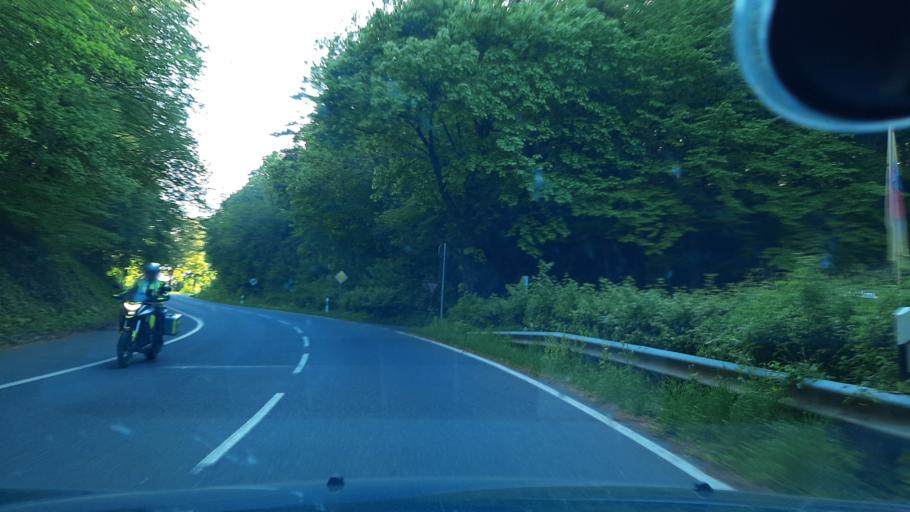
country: DE
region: North Rhine-Westphalia
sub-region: Regierungsbezirk Koln
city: Mechernich
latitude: 50.5444
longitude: 6.6598
